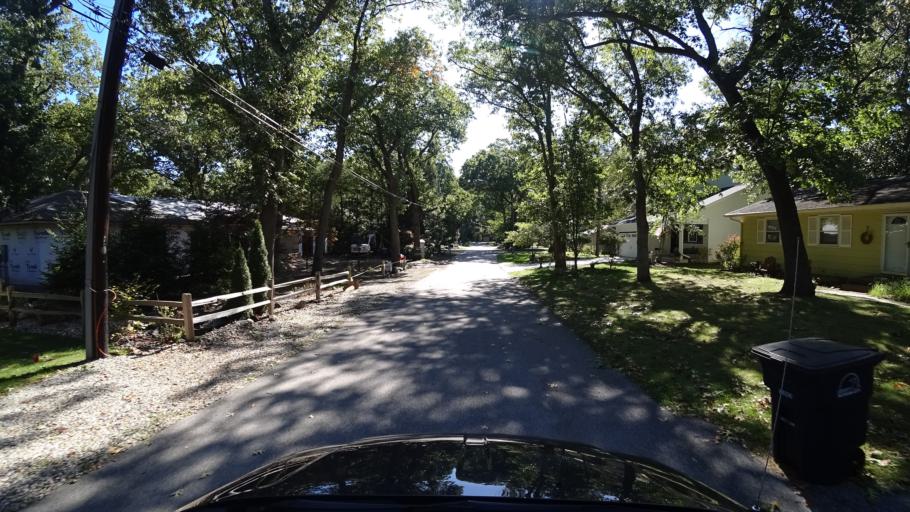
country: US
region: Indiana
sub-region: LaPorte County
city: Long Beach
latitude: 41.7510
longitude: -86.8321
